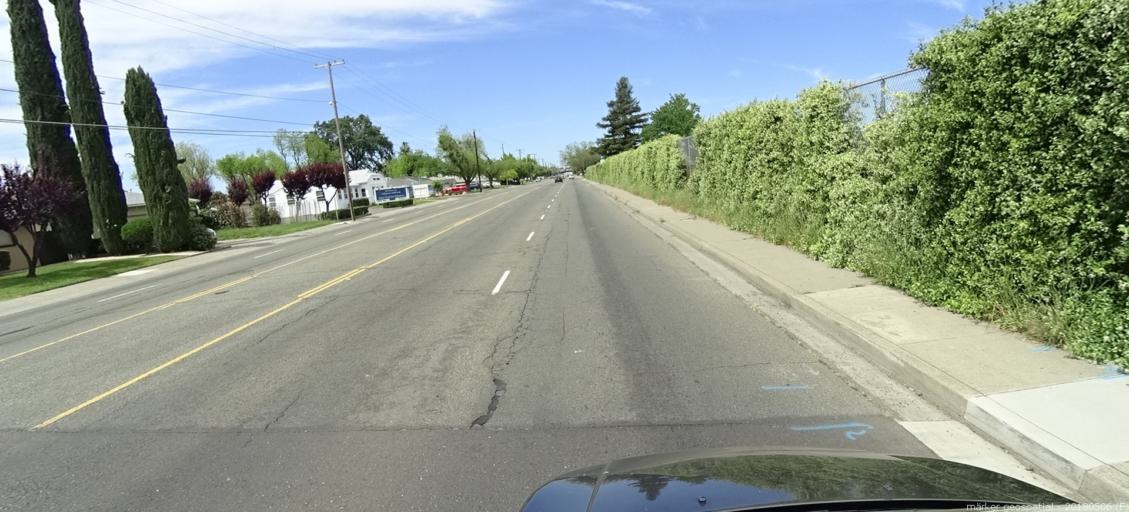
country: US
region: California
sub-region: Sacramento County
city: Florin
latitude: 38.5415
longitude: -121.4278
